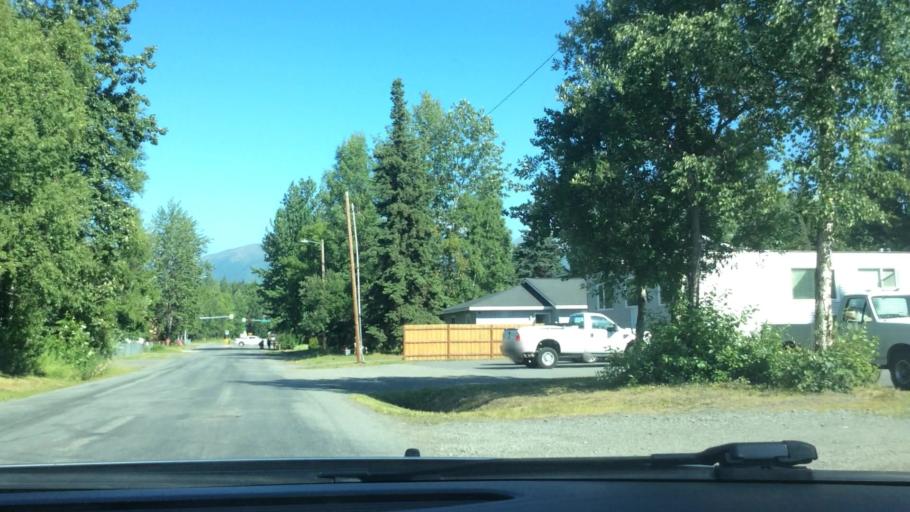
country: US
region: Alaska
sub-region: Anchorage Municipality
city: Anchorage
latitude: 61.1989
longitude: -149.7826
